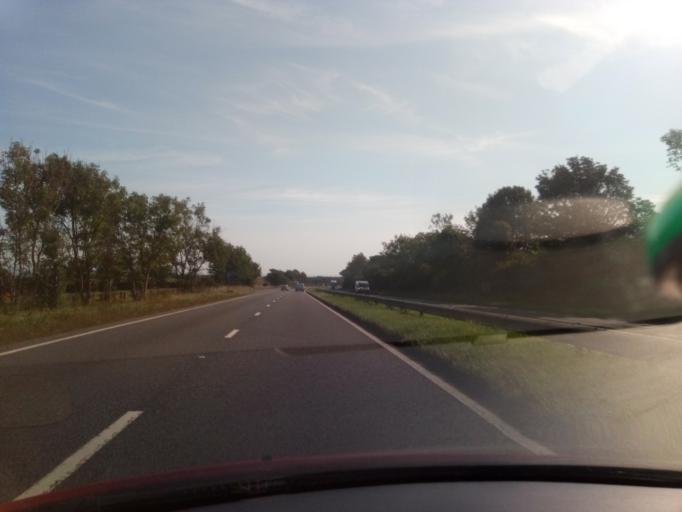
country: GB
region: England
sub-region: Sunderland
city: Ryhope
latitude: 54.8484
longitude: -1.3848
